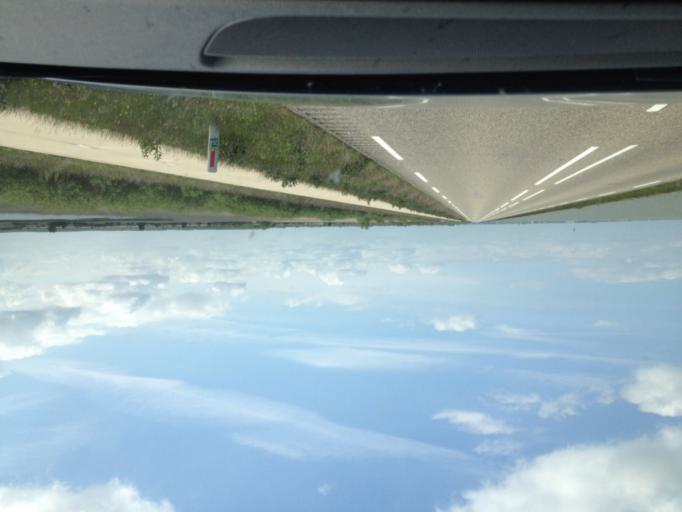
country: NL
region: Flevoland
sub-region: Gemeente Lelystad
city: Lelystad
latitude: 52.4711
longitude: 5.3418
